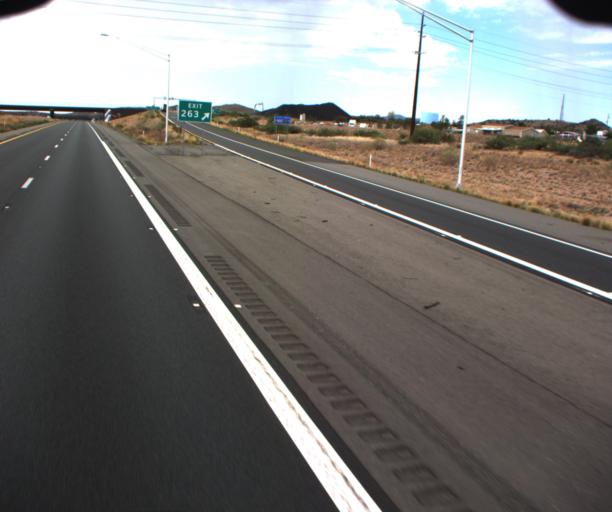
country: US
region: Arizona
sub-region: Yavapai County
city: Cordes Lakes
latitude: 34.3376
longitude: -112.1192
